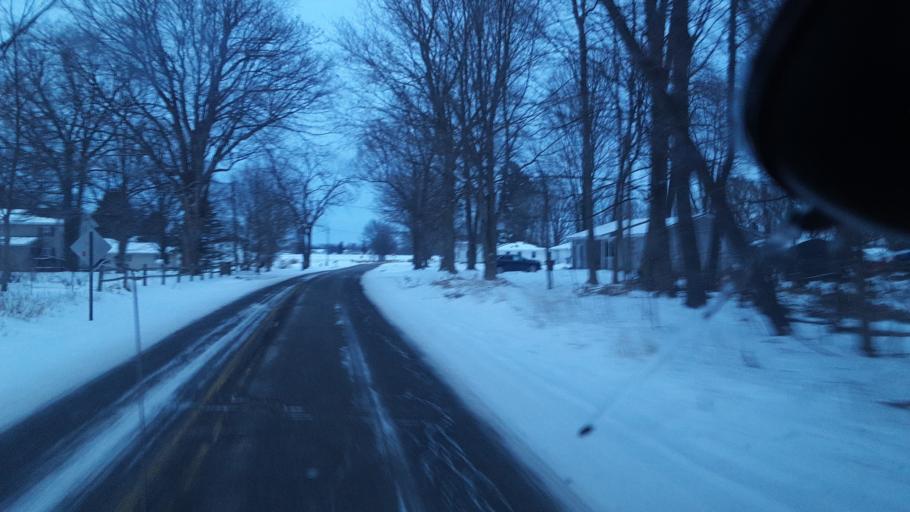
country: US
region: Michigan
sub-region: Ingham County
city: Stockbridge
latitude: 42.4072
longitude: -84.2727
